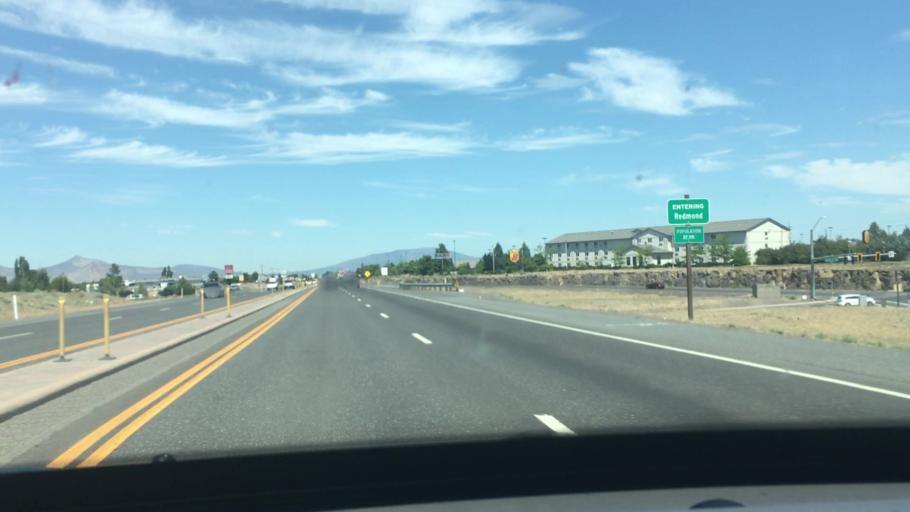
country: US
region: Oregon
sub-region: Deschutes County
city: Redmond
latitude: 44.2416
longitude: -121.1941
